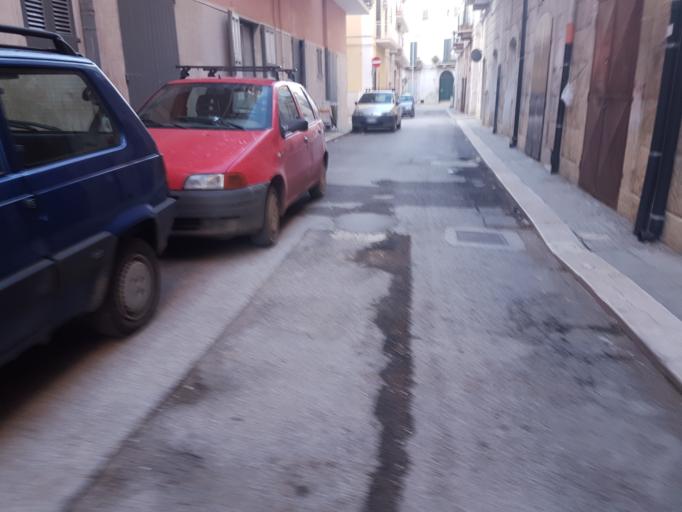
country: IT
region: Apulia
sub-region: Provincia di Bari
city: Corato
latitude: 41.1550
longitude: 16.4065
